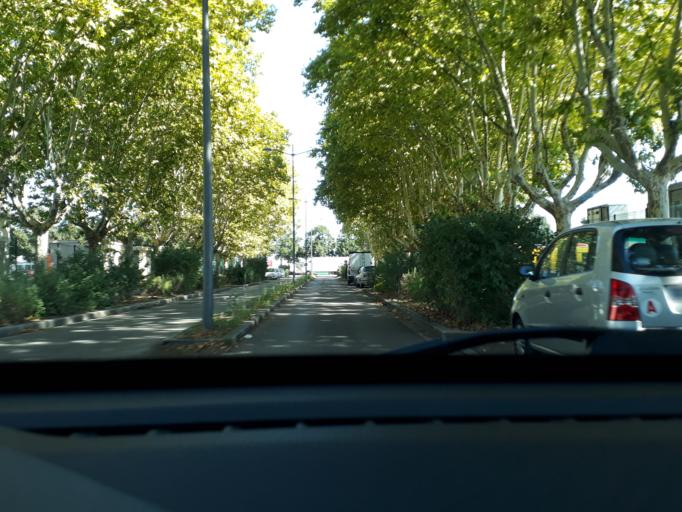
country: FR
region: Rhone-Alpes
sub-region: Departement du Rhone
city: Bron
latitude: 45.7068
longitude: 4.9043
